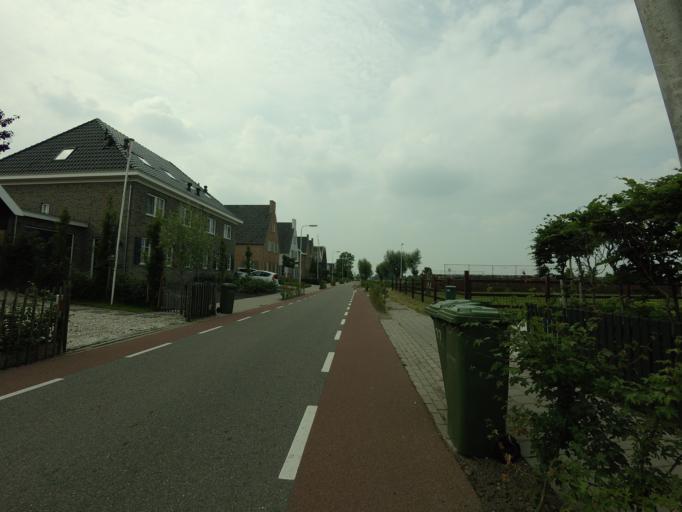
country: NL
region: South Holland
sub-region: Molenwaard
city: Nieuw-Lekkerland
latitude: 51.9496
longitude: 4.7011
